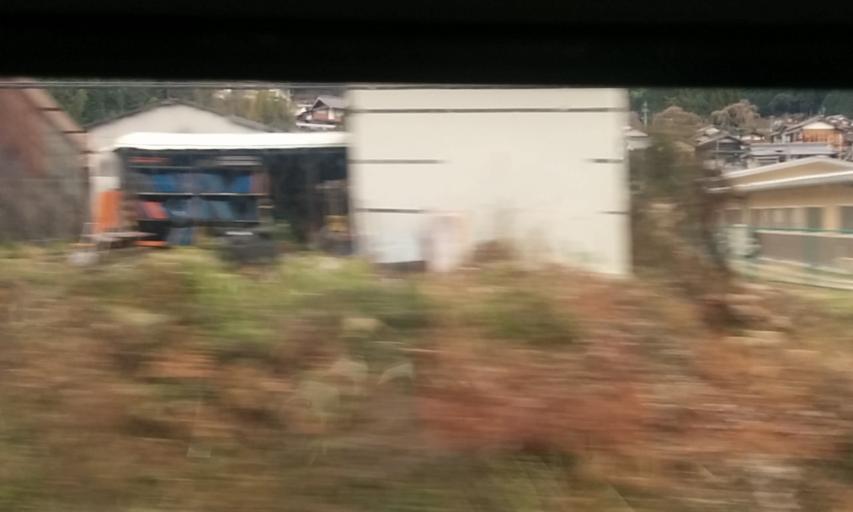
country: JP
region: Gifu
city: Nakatsugawa
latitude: 35.6079
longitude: 137.6096
